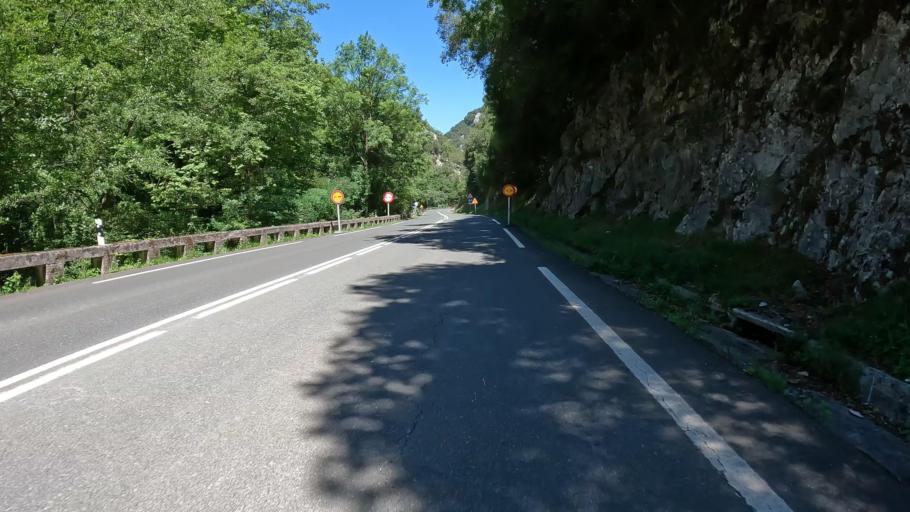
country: ES
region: Basque Country
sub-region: Provincia de Guipuzcoa
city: Oreja
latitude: 43.0761
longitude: -2.0163
